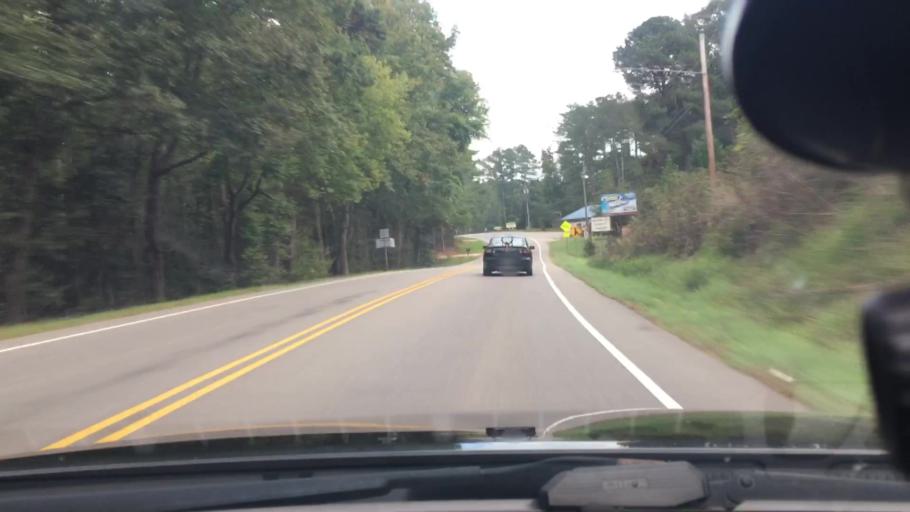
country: US
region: North Carolina
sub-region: Moore County
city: Carthage
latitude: 35.3583
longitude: -79.4336
